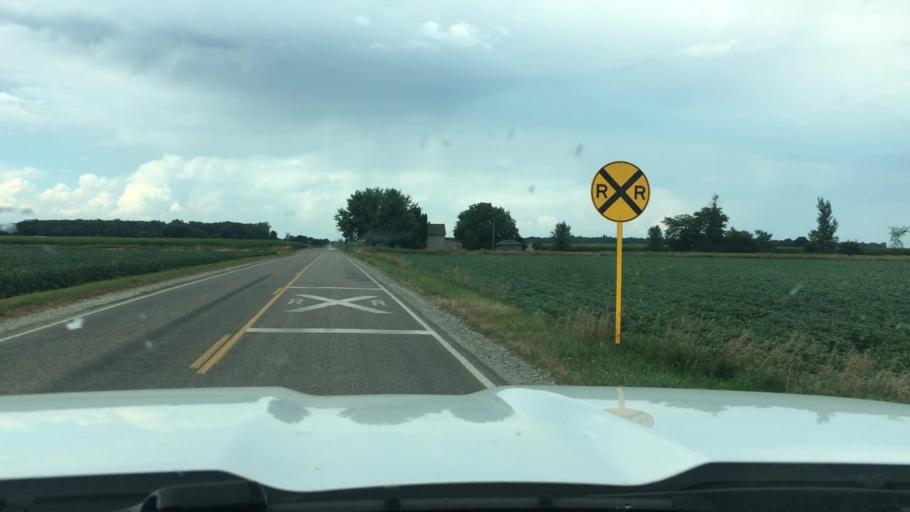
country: US
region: Michigan
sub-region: Montcalm County
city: Carson City
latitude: 43.1821
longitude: -84.7781
